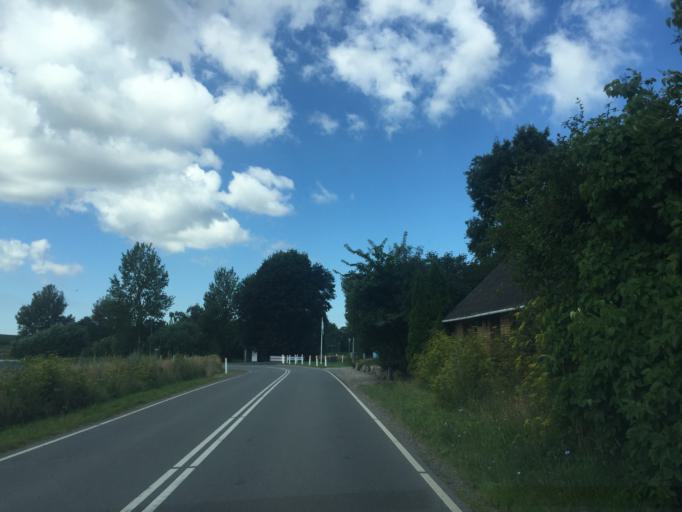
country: DK
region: South Denmark
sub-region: Nordfyns Kommune
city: Otterup
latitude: 55.5705
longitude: 10.3686
